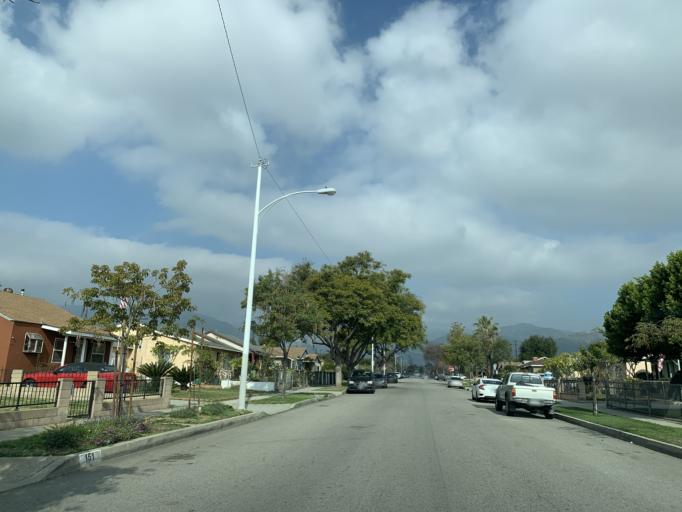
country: US
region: California
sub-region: Los Angeles County
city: Azusa
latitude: 34.1233
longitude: -117.9102
